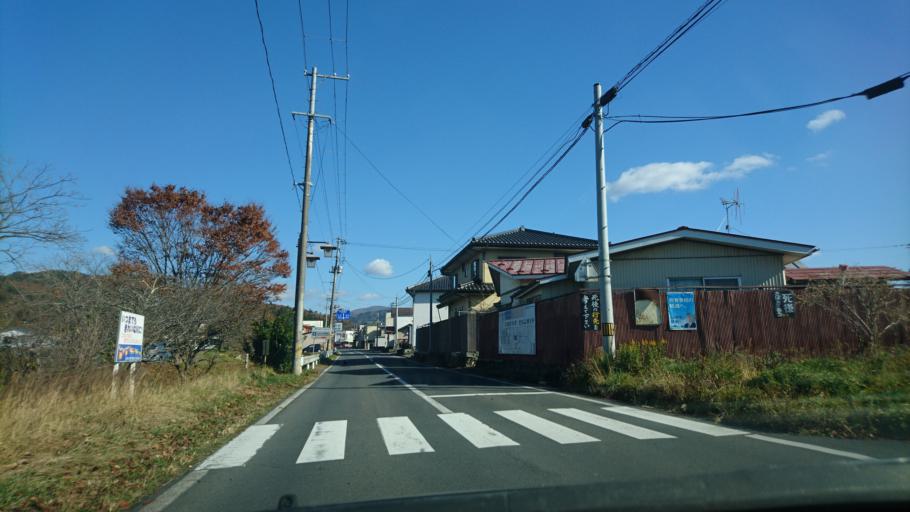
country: JP
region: Iwate
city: Ichinoseki
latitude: 39.0132
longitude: 141.3941
